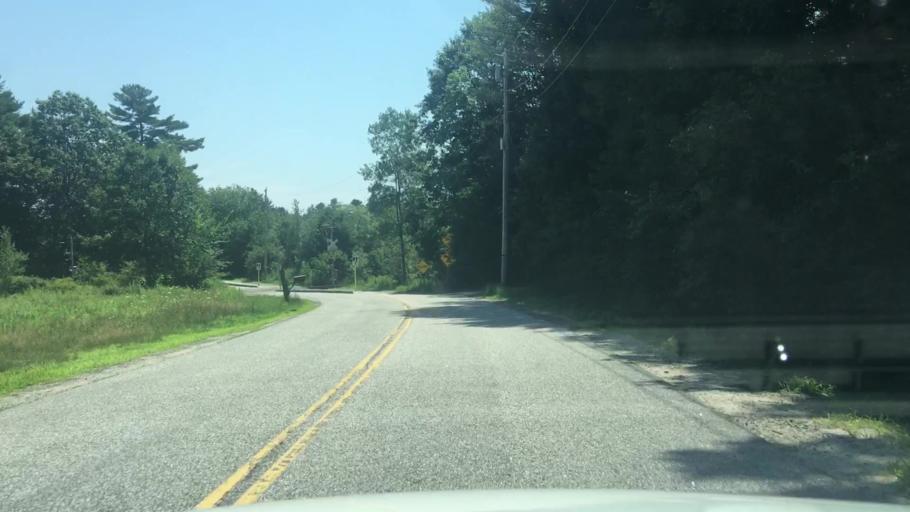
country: US
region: Maine
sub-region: Cumberland County
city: Falmouth
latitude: 43.7520
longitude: -70.2753
